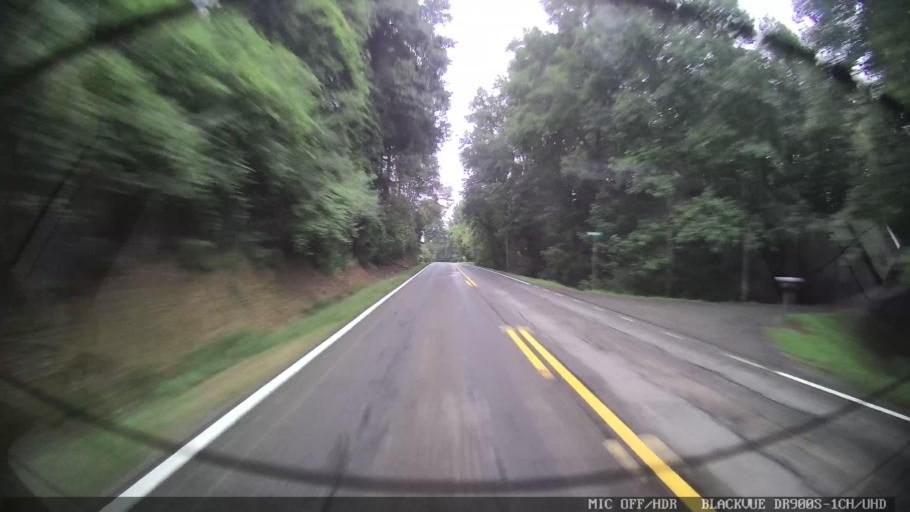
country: US
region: Georgia
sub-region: Gilmer County
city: Ellijay
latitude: 34.7443
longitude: -84.5280
